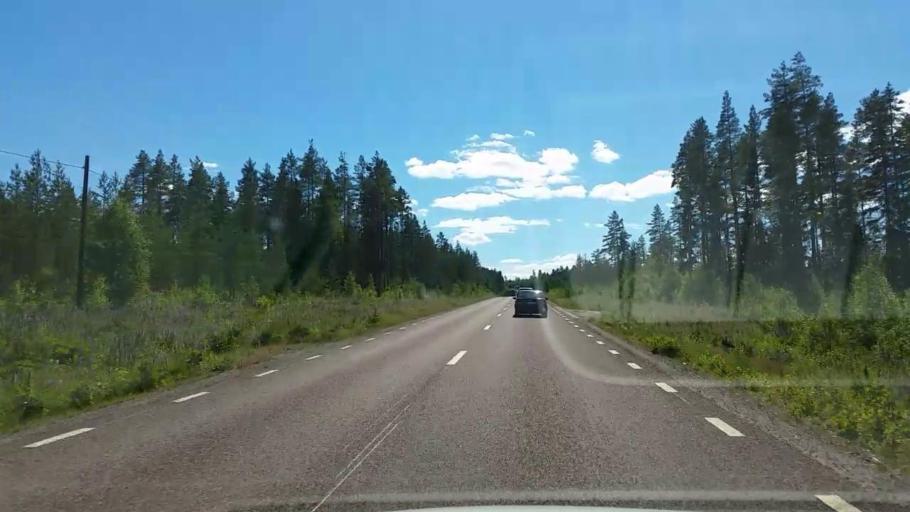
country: SE
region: Gaevleborg
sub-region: Ovanakers Kommun
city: Edsbyn
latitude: 61.2648
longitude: 15.8893
